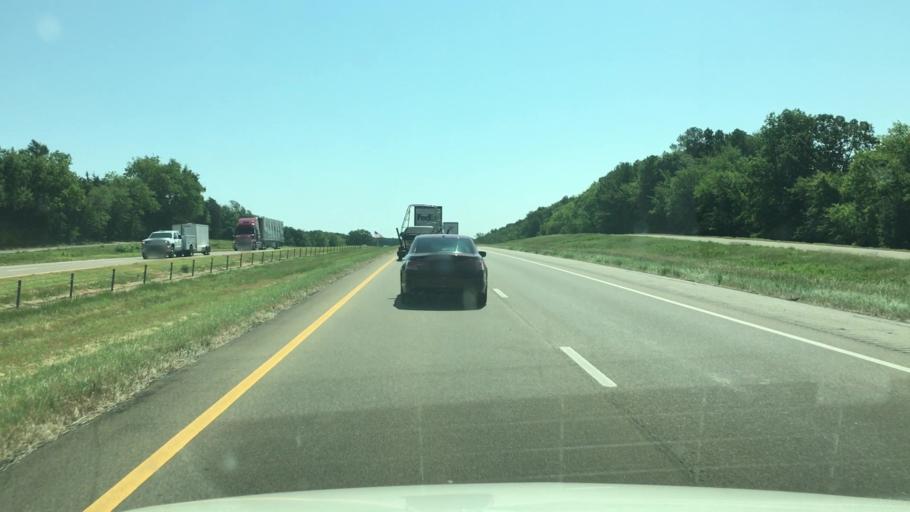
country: US
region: Texas
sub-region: Titus County
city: Mount Pleasant
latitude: 33.1596
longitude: -95.0896
